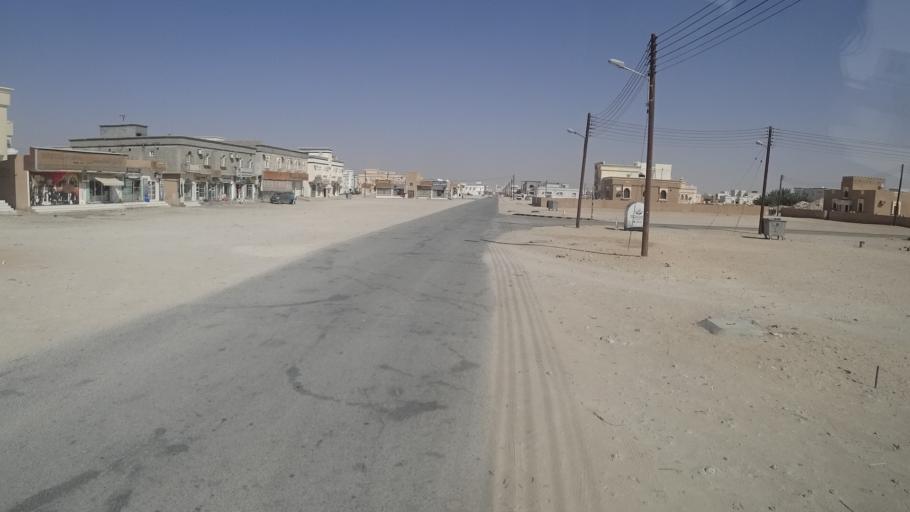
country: YE
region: Al Mahrah
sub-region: Shahan
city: Shihan as Sufla
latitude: 17.8419
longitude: 52.6573
